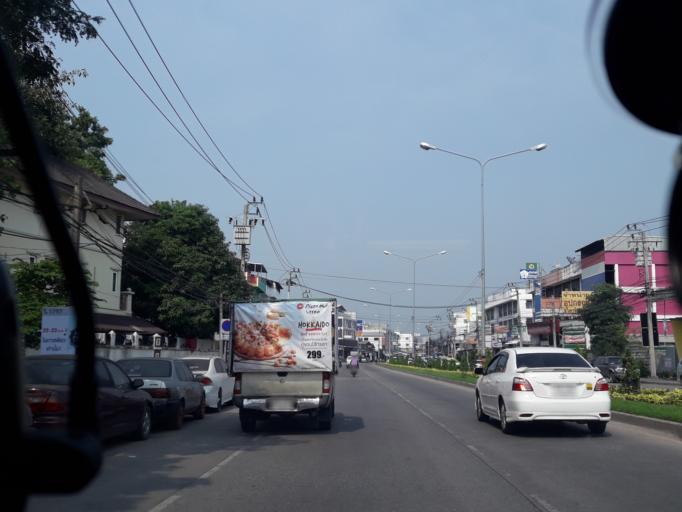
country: TH
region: Bangkok
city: Khan Na Yao
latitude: 13.8327
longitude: 100.6986
